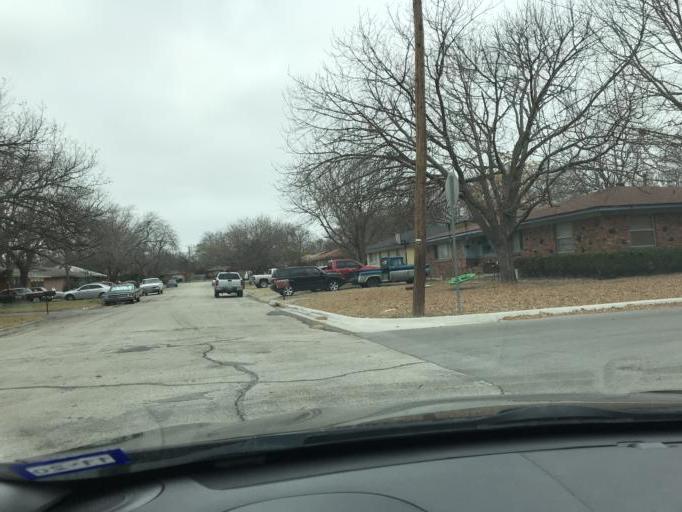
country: US
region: Texas
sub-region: Denton County
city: Denton
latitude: 33.2249
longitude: -97.1517
